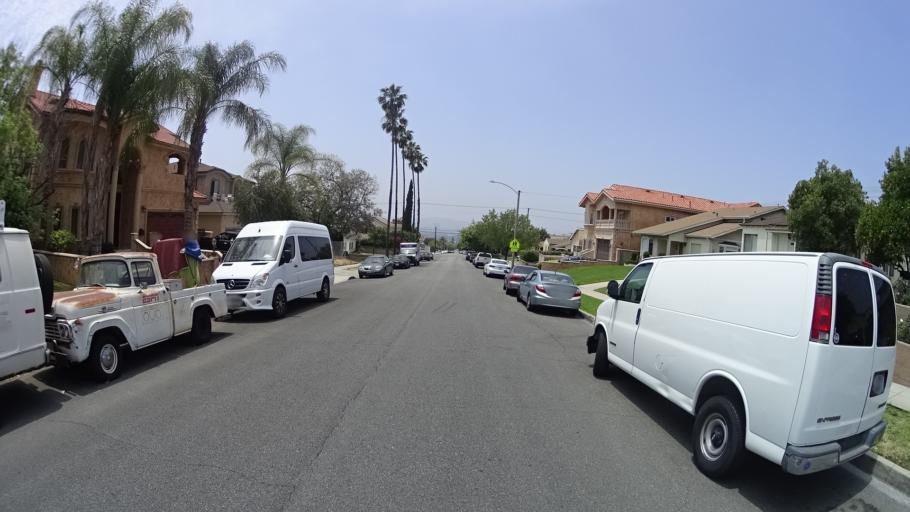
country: US
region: California
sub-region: Los Angeles County
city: Burbank
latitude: 34.1923
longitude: -118.3053
